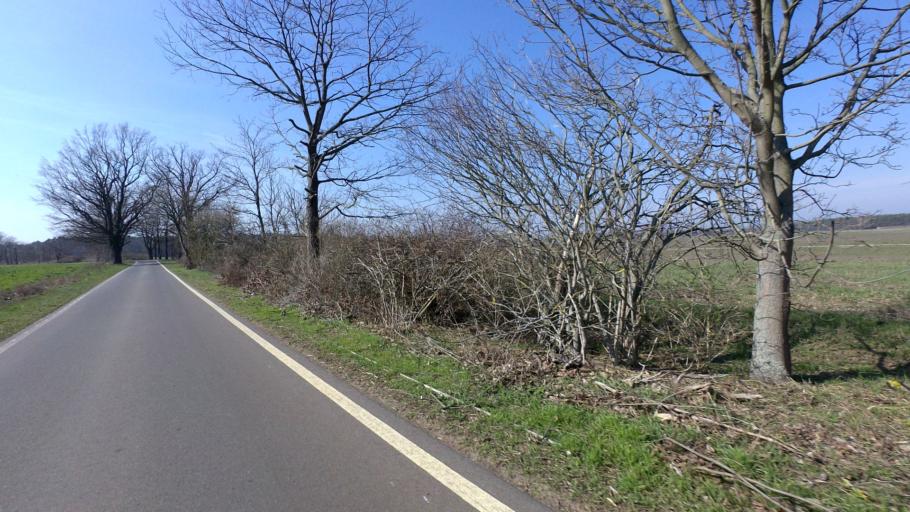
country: DE
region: Brandenburg
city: Baruth
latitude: 52.0717
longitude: 13.4730
